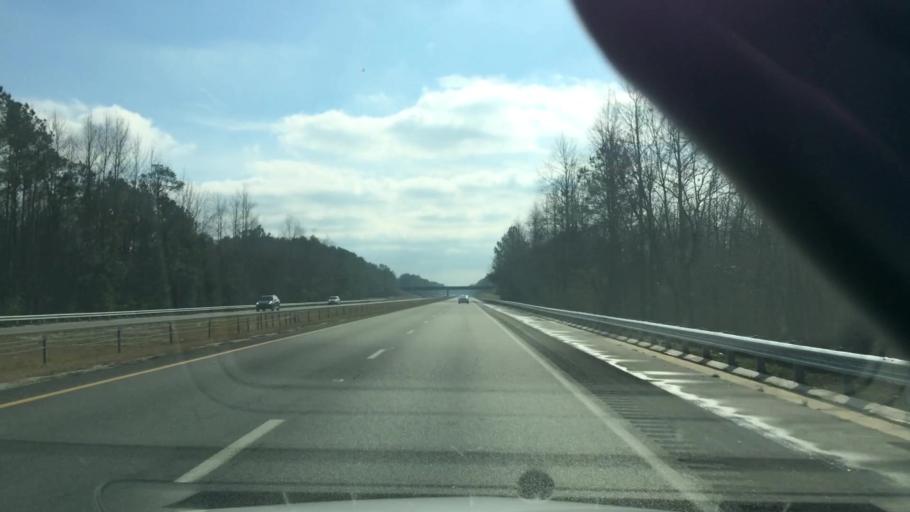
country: US
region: North Carolina
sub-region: Pender County
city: Rocky Point
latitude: 34.4849
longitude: -77.8784
